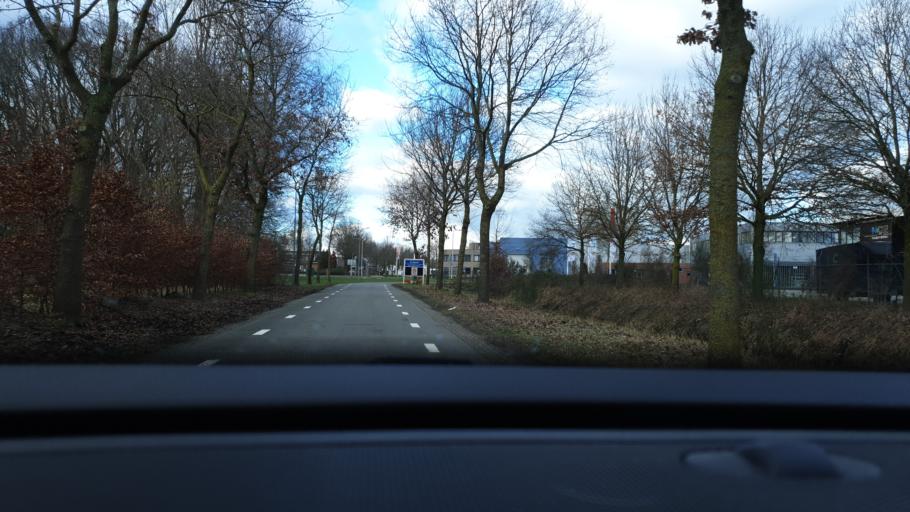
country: NL
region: Gelderland
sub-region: Gemeente Bronckhorst
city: Zelhem
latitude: 51.9974
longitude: 6.3549
